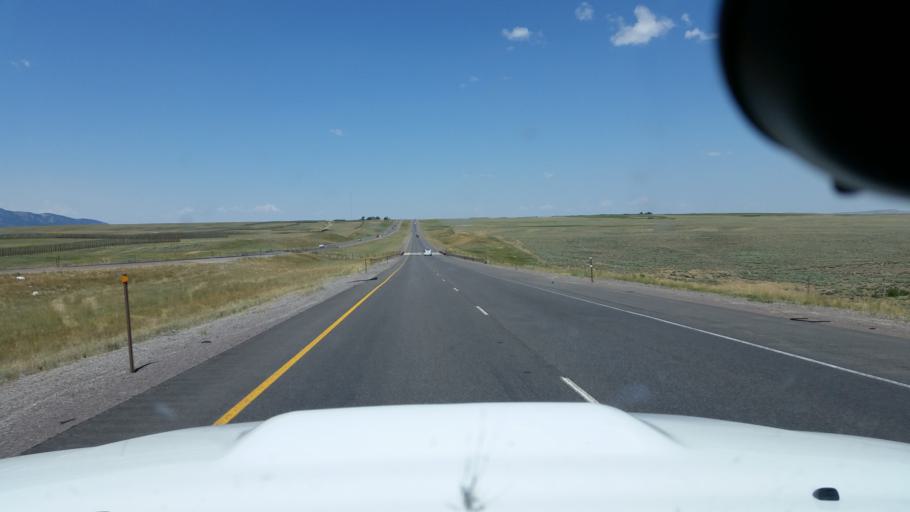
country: US
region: Wyoming
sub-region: Carbon County
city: Saratoga
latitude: 41.6553
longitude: -106.3420
